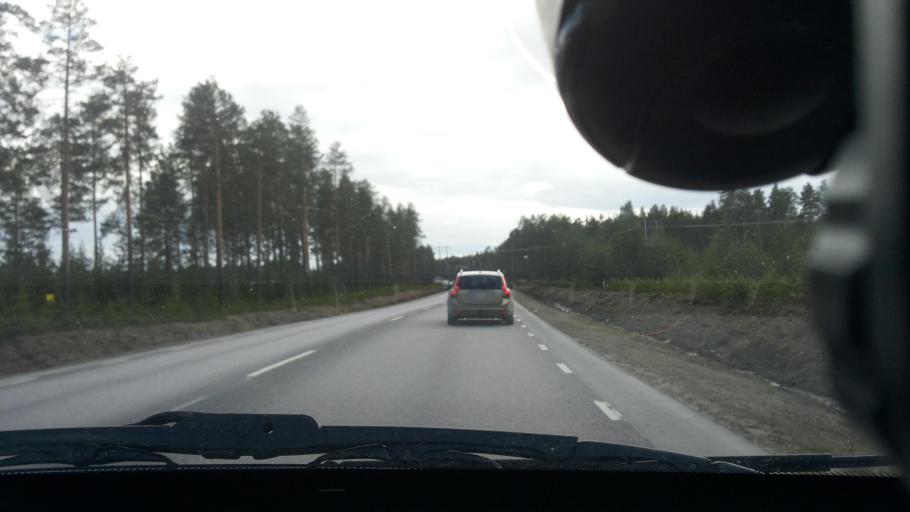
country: SE
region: Norrbotten
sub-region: Lulea Kommun
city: Gammelstad
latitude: 65.6121
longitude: 22.0431
